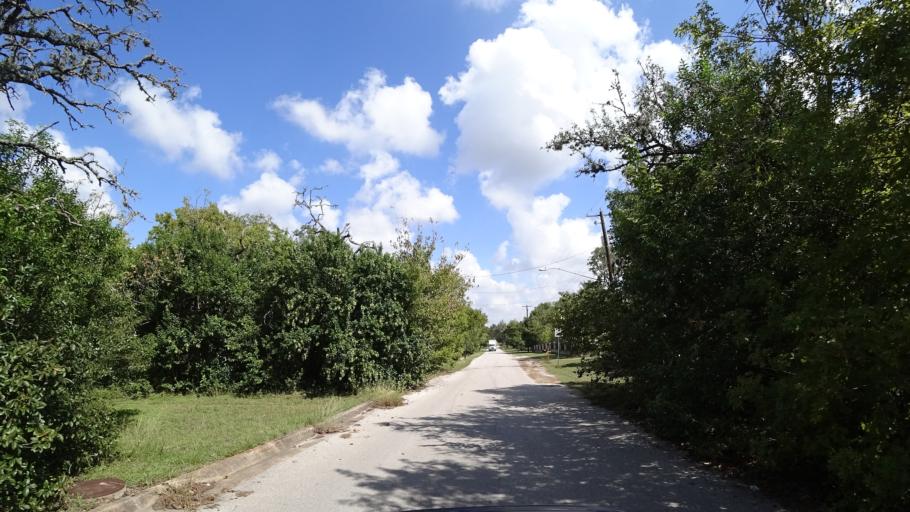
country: US
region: Texas
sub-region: Travis County
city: Manchaca
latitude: 30.1933
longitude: -97.8051
